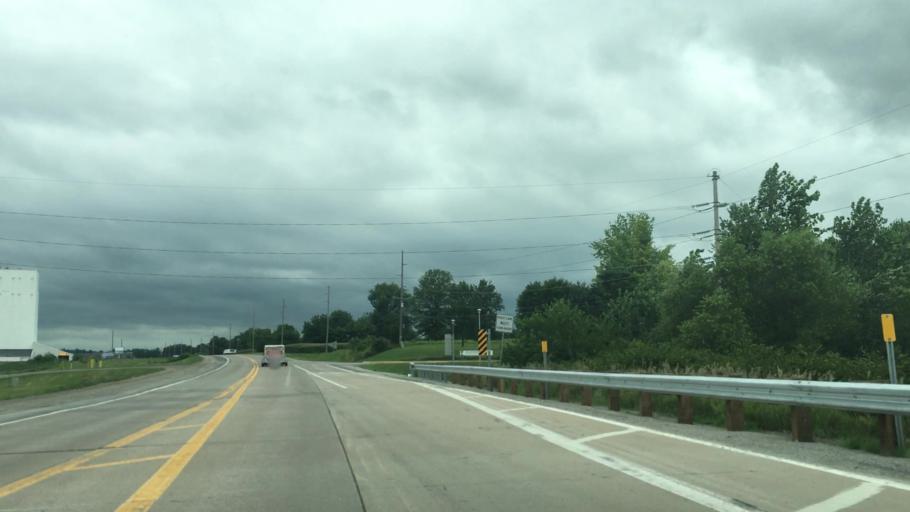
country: US
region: Iowa
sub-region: Johnson County
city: Tiffin
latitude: 41.7016
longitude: -91.6308
